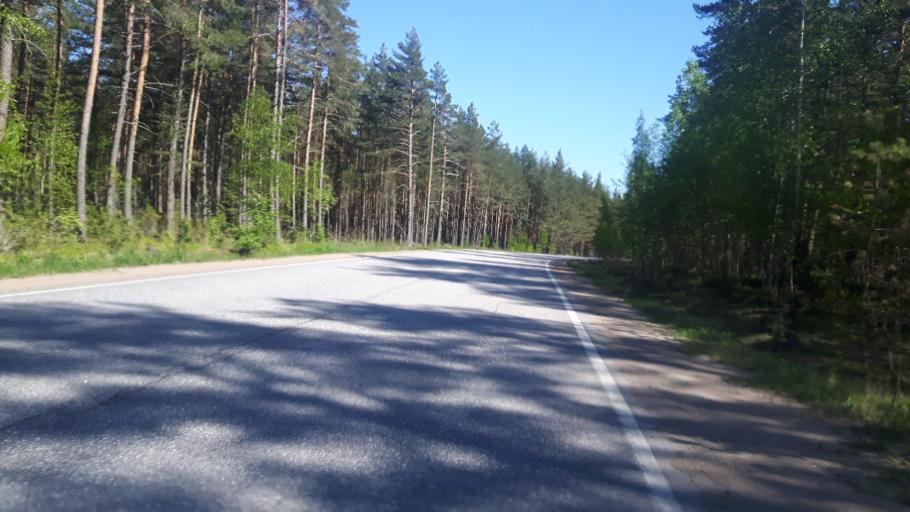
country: RU
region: Leningrad
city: Glebychevo
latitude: 60.2792
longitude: 28.8937
